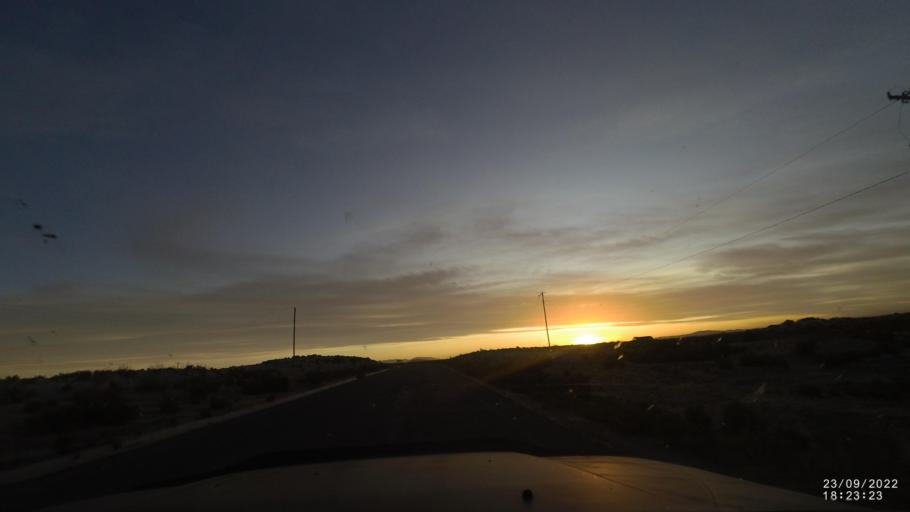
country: BO
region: Oruro
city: Challapata
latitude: -19.2946
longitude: -67.1024
